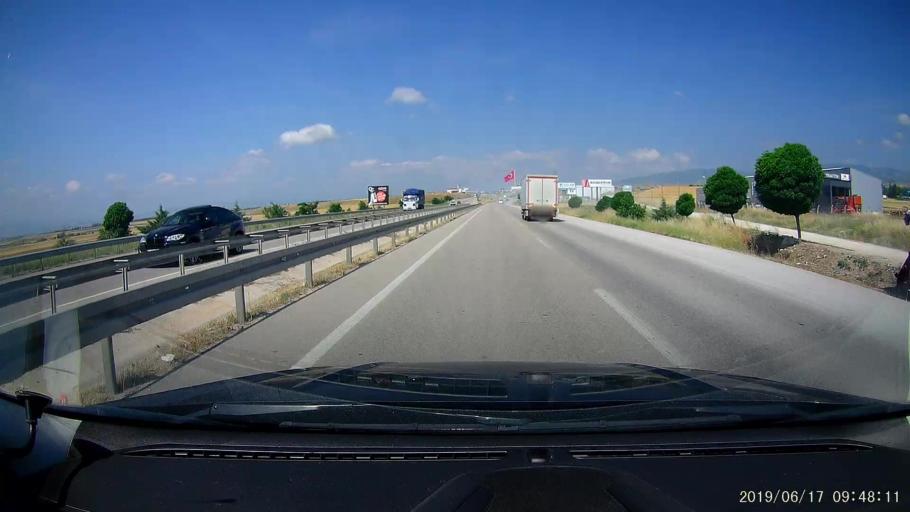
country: TR
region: Amasya
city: Merzifon
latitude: 40.8751
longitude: 35.5599
